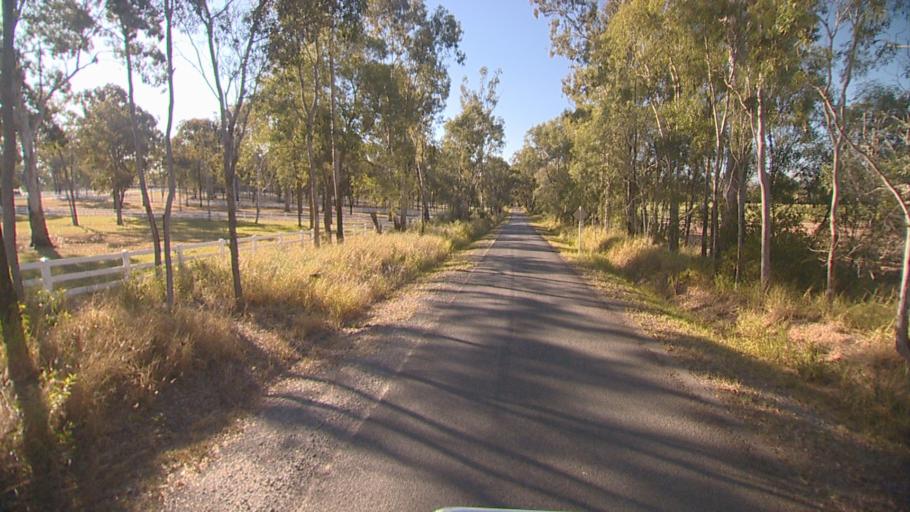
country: AU
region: Queensland
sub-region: Logan
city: North Maclean
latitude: -27.7777
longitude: 153.0376
